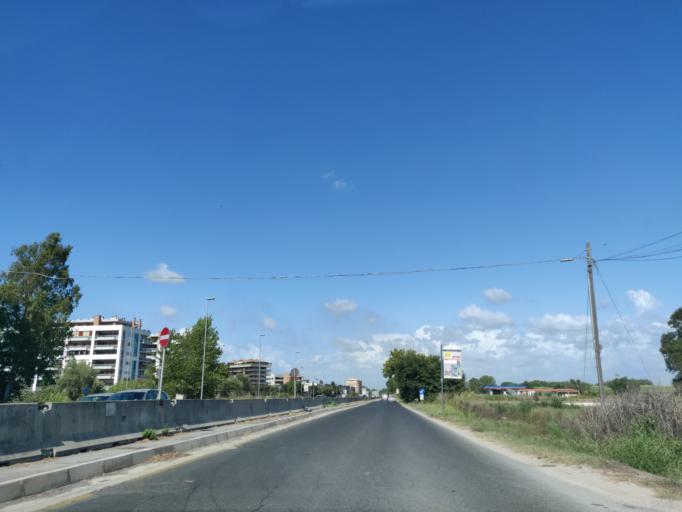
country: IT
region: Latium
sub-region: Citta metropolitana di Roma Capitale
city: Npp 23 (Parco Leonardo)
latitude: 41.7939
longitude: 12.2941
